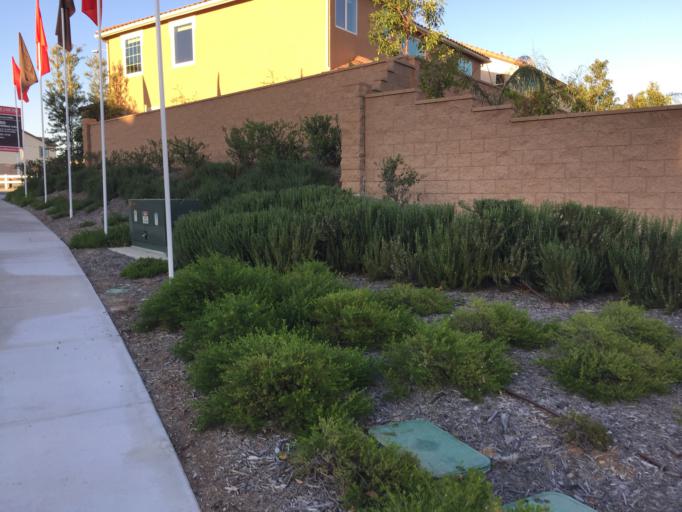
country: US
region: California
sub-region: Riverside County
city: Home Gardens
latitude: 33.8958
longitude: -117.4640
